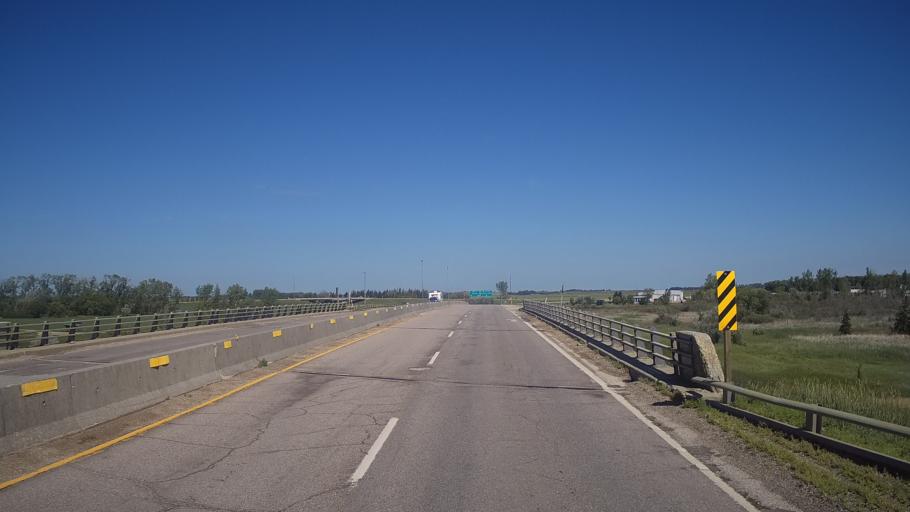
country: CA
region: Manitoba
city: Portage la Prairie
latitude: 49.9673
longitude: -98.3569
